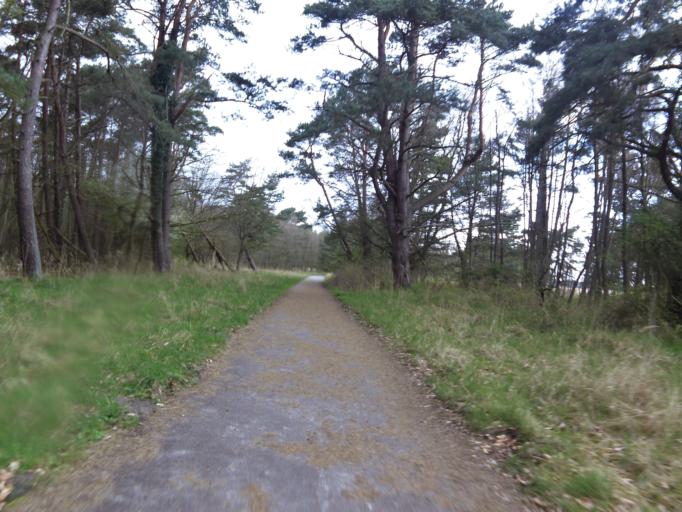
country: DE
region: Mecklenburg-Vorpommern
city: Ostseebad Prerow
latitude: 54.4678
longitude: 12.5217
